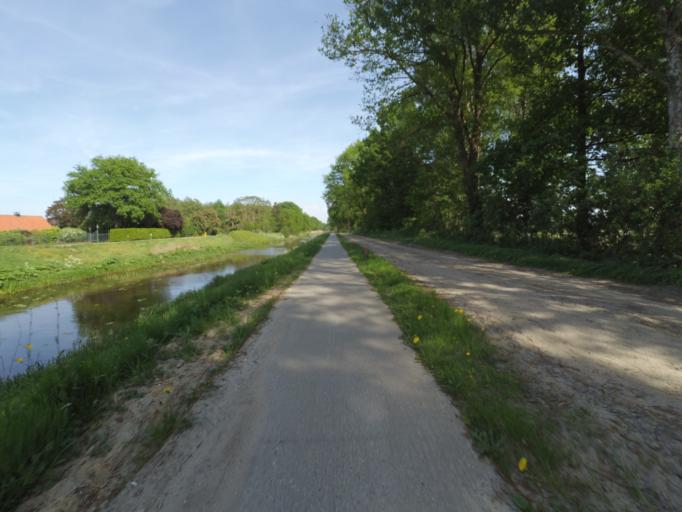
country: NL
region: Overijssel
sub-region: Gemeente Borne
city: Borne
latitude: 52.3636
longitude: 6.7319
